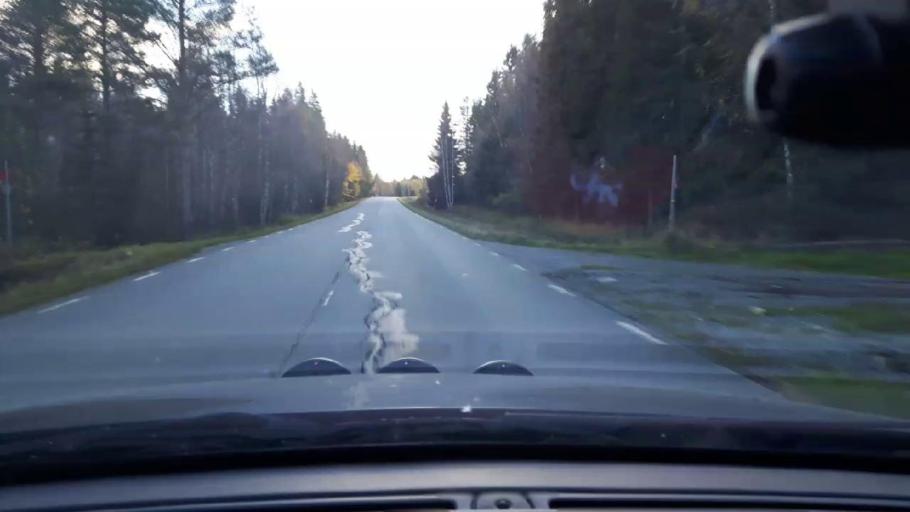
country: SE
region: Jaemtland
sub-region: Bergs Kommun
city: Hoverberg
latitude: 63.0277
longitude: 14.3448
